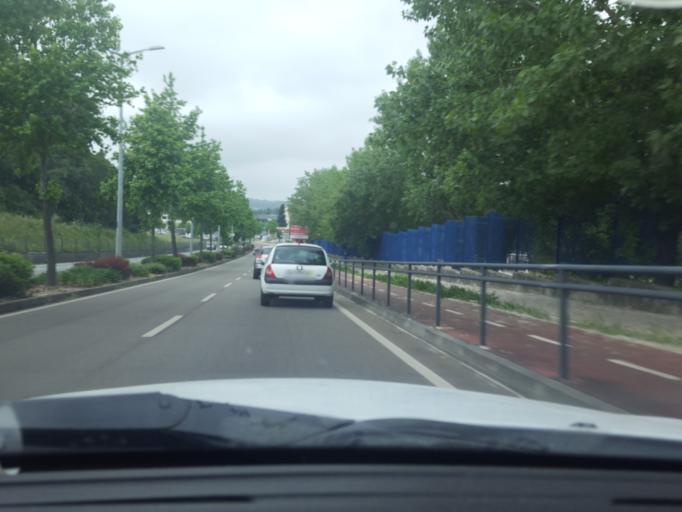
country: PT
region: Leiria
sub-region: Leiria
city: Leiria
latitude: 39.7374
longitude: -8.8132
